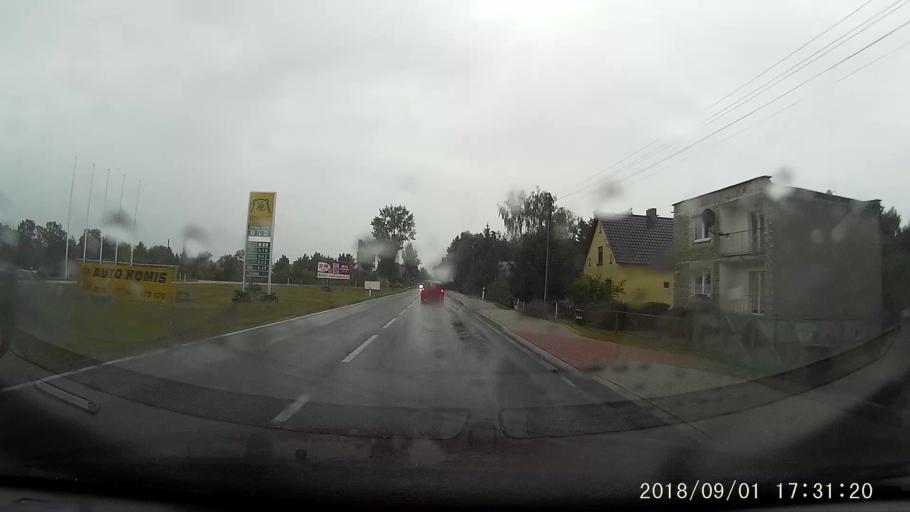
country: PL
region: Lubusz
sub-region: Powiat zaganski
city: Zagan
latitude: 51.6339
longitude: 15.3246
